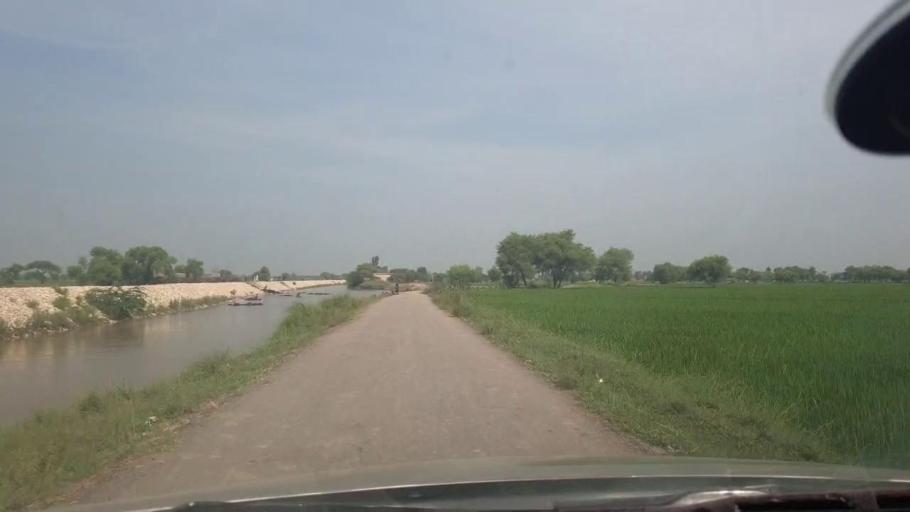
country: PK
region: Sindh
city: Jacobabad
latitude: 28.2913
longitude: 68.4807
